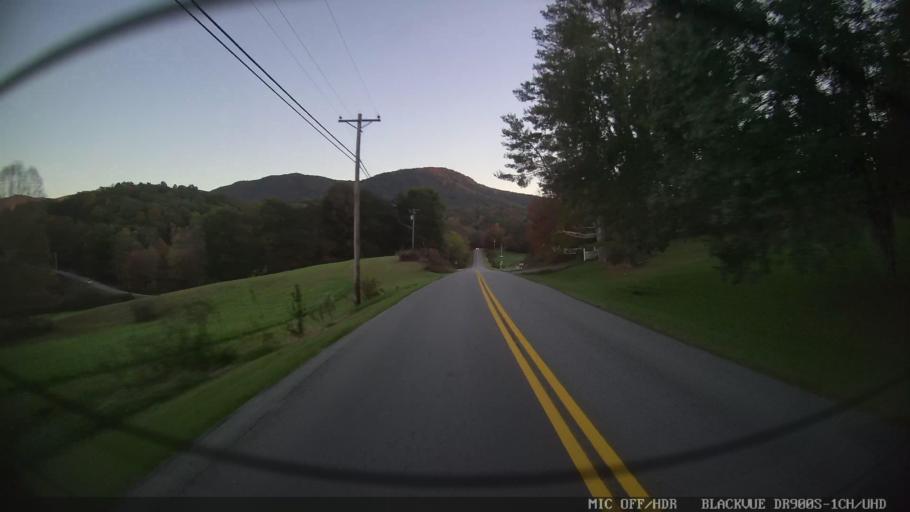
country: US
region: Georgia
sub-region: Union County
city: Blairsville
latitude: 34.9054
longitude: -83.8658
